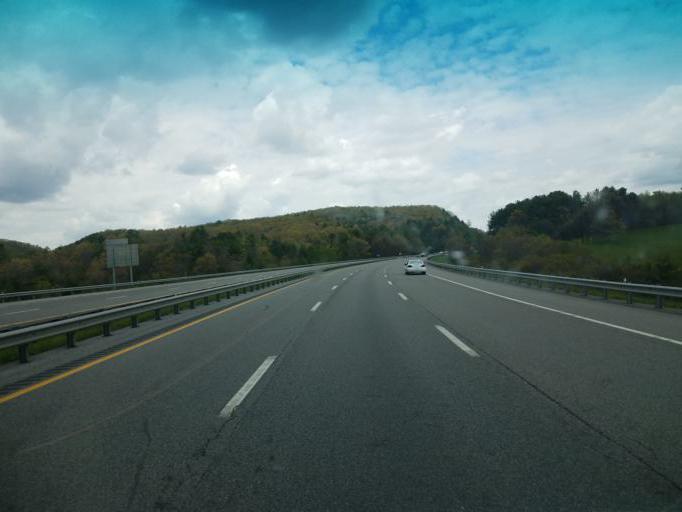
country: US
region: Virginia
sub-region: Bland County
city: Bland
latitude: 37.1052
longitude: -81.1289
